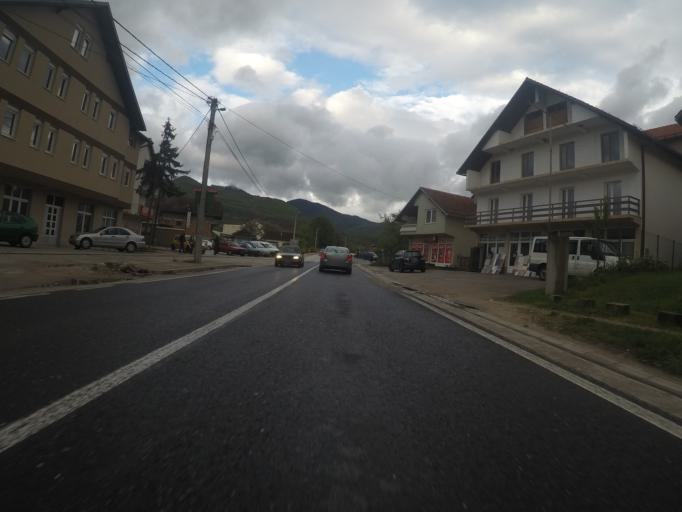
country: BA
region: Federation of Bosnia and Herzegovina
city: Konjic
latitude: 43.6837
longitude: 17.8953
